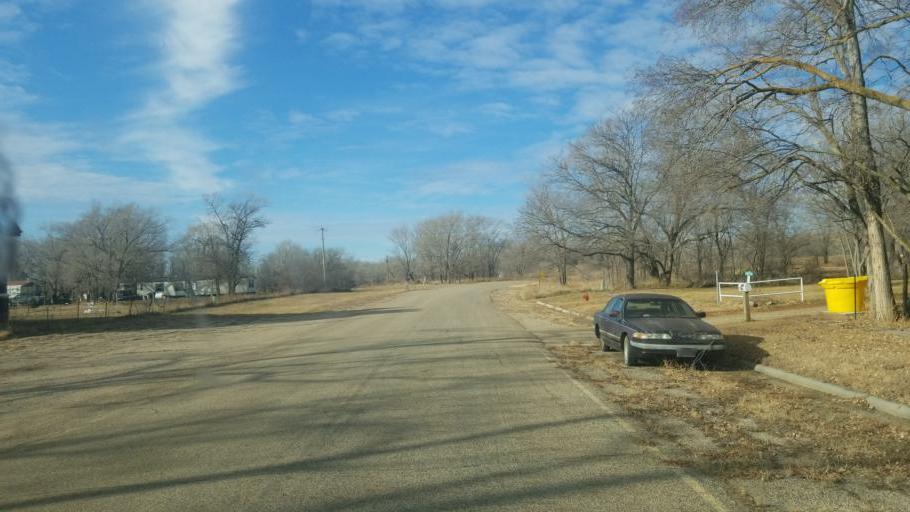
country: US
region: South Dakota
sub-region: Charles Mix County
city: Wagner
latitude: 42.9231
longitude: -98.3883
